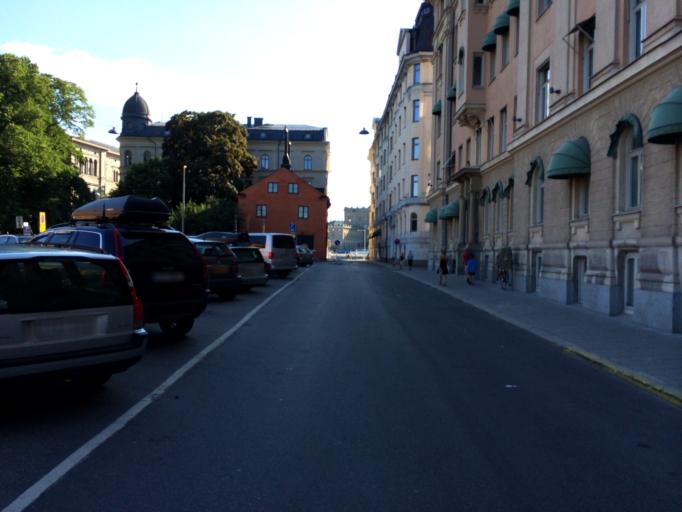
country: SE
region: Stockholm
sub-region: Stockholms Kommun
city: OEstermalm
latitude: 59.3299
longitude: 18.0784
